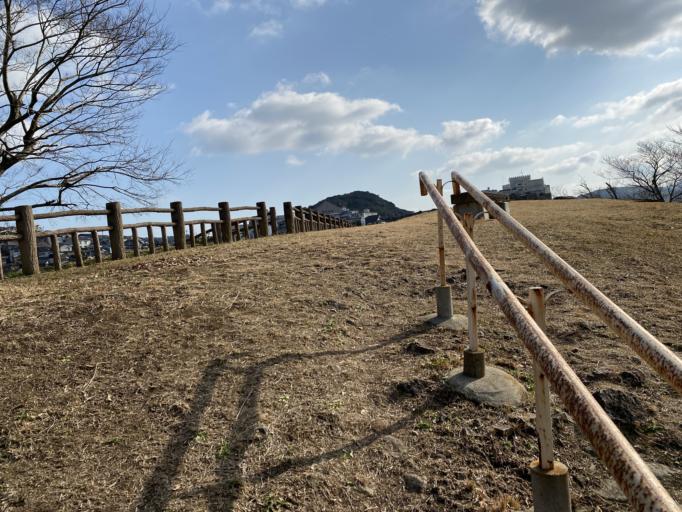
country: JP
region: Nagasaki
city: Nagasaki-shi
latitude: 32.7447
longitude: 129.8865
